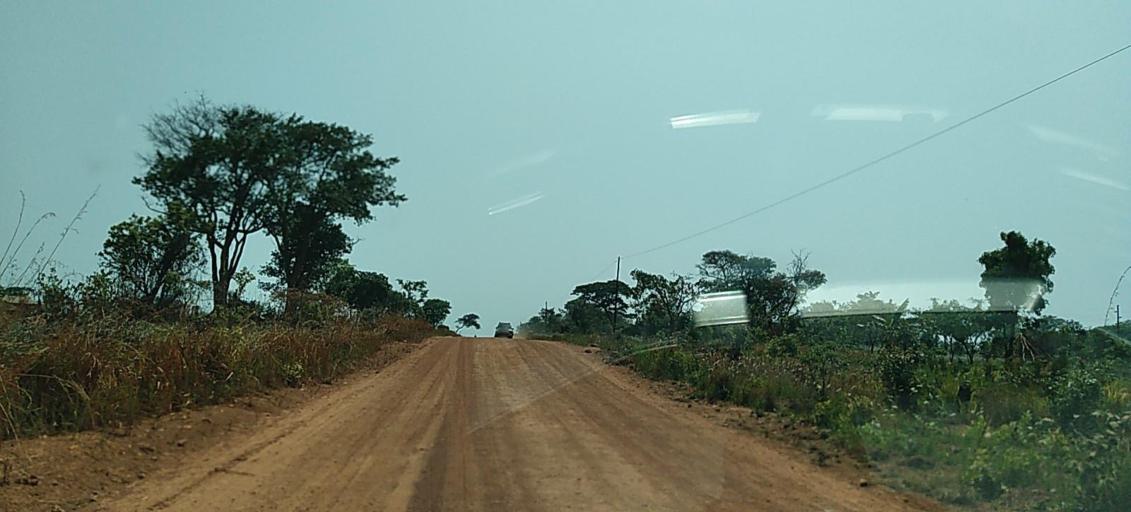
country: ZM
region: North-Western
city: Kansanshi
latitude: -12.0052
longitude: 26.5822
